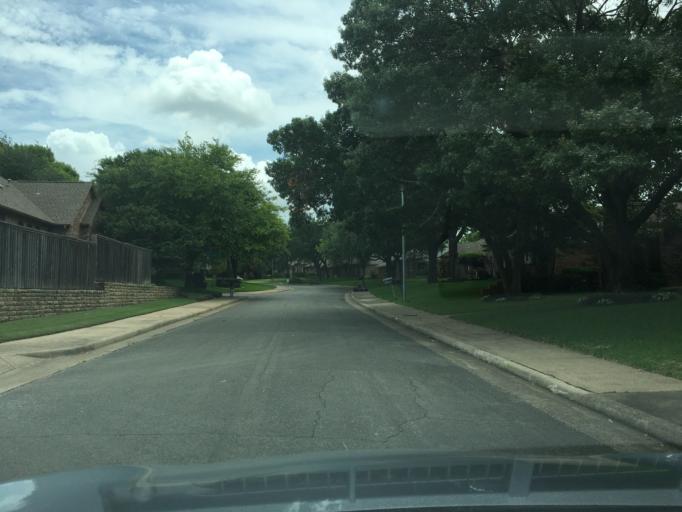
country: US
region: Texas
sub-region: Dallas County
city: Richardson
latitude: 32.9156
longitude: -96.7151
